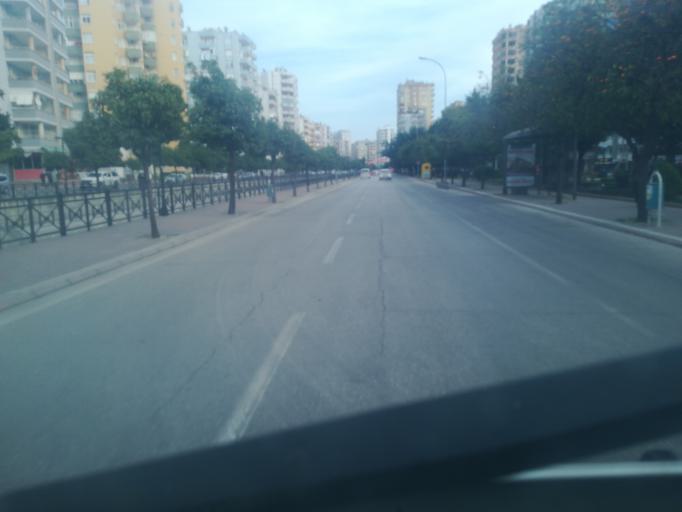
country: TR
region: Adana
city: Adana
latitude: 37.0304
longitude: 35.2967
